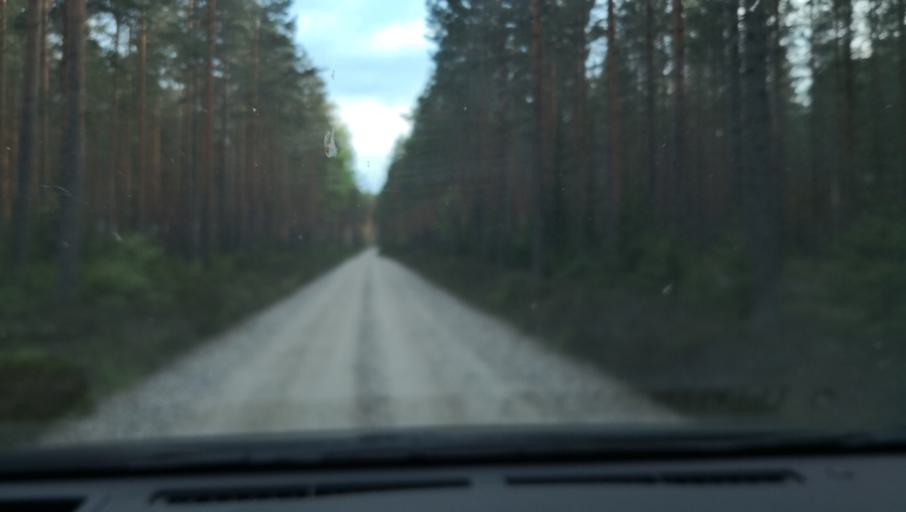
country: SE
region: Vaestmanland
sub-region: Skinnskattebergs Kommun
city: Skinnskatteberg
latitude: 59.8007
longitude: 15.4924
